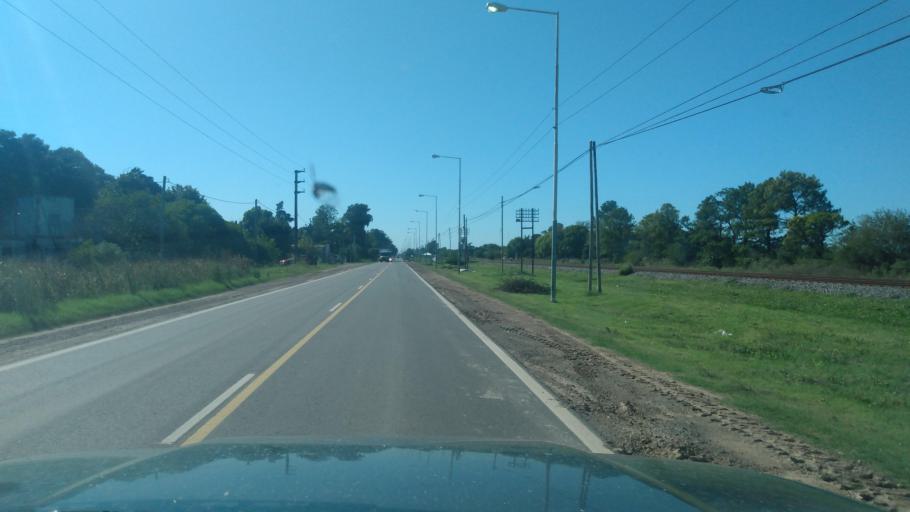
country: AR
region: Buenos Aires
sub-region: Partido de General Rodriguez
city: General Rodriguez
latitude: -34.5959
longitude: -59.0075
